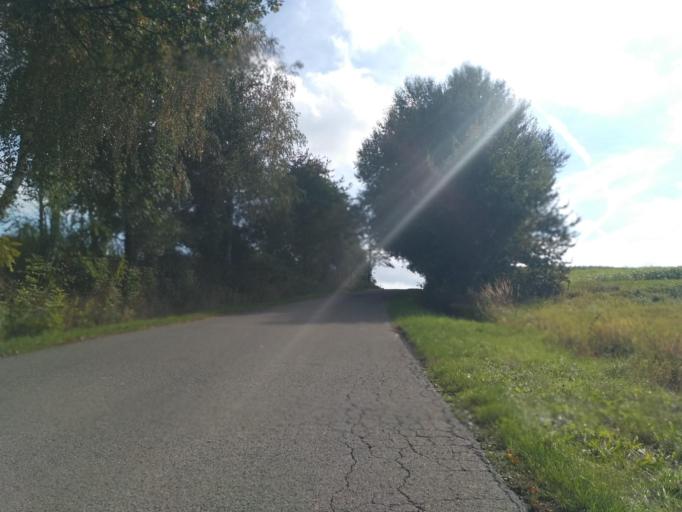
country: PL
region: Subcarpathian Voivodeship
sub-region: Powiat ropczycko-sedziszowski
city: Wielopole Skrzynskie
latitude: 49.9285
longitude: 21.5649
